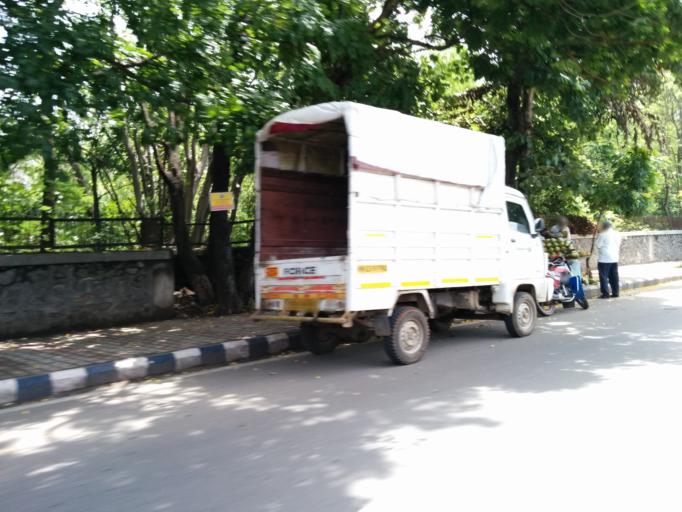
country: IN
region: Maharashtra
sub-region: Pune Division
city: Pune
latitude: 18.5329
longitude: 73.9183
